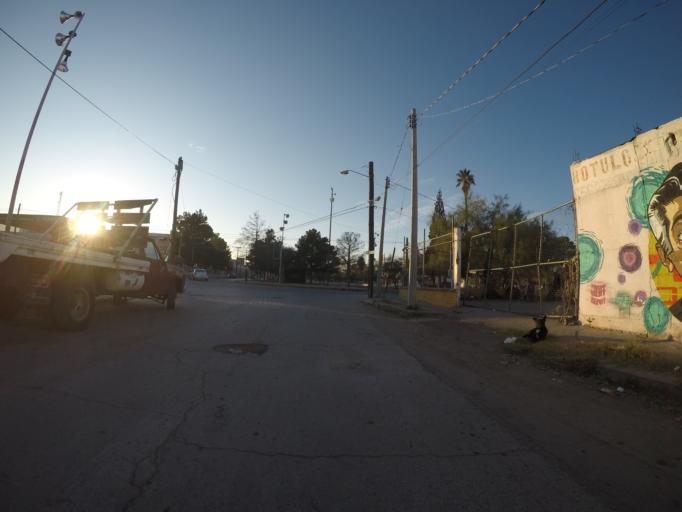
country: MX
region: Chihuahua
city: Ciudad Juarez
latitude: 31.7347
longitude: -106.4778
